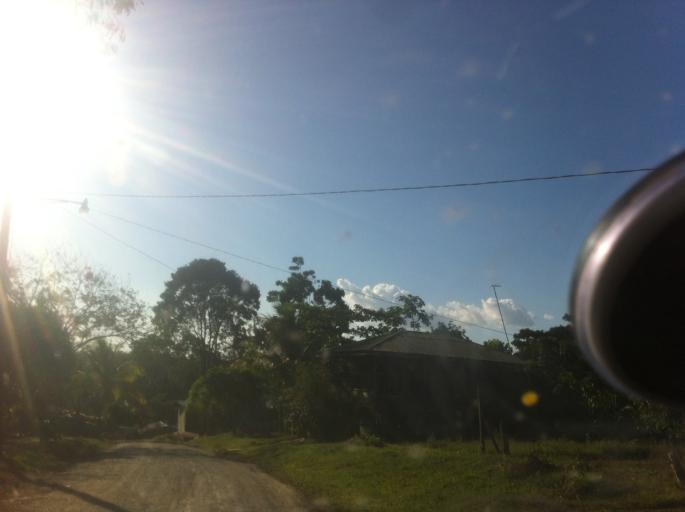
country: CR
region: Alajuela
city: Los Chiles
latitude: 11.0433
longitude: -84.4708
